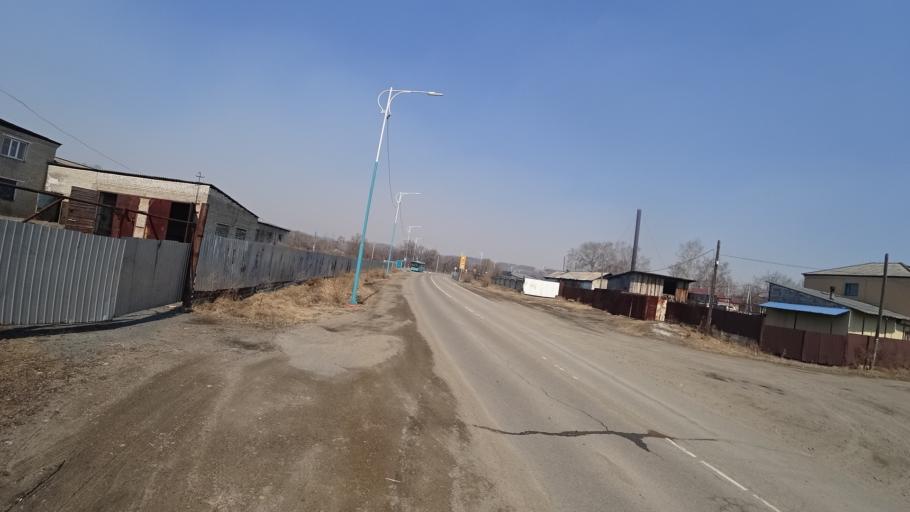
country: RU
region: Amur
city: Novobureyskiy
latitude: 49.7915
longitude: 129.9050
